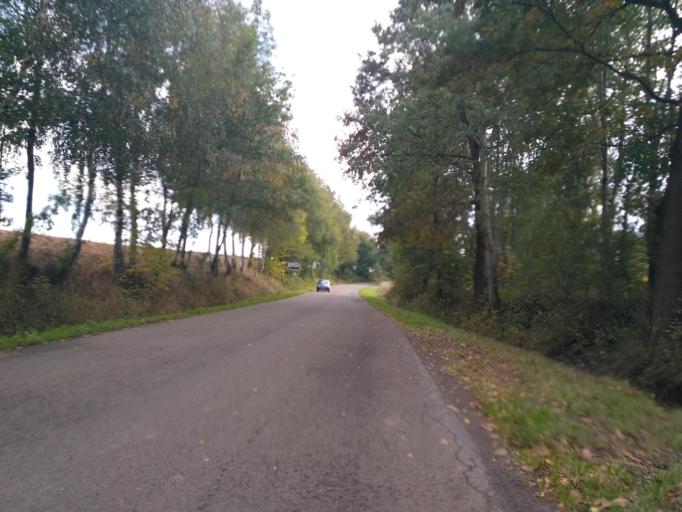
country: PL
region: Subcarpathian Voivodeship
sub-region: Powiat ropczycko-sedziszowski
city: Wielopole Skrzynskie
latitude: 49.9294
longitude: 21.5643
